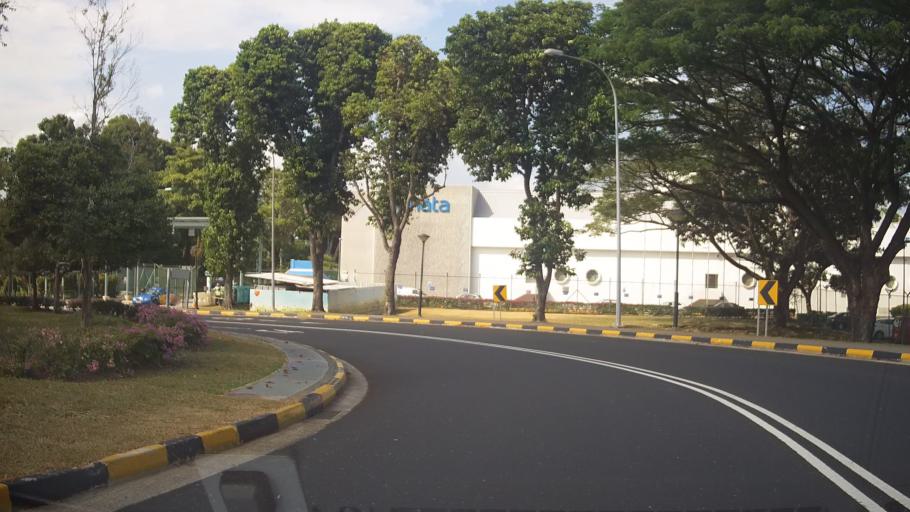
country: SG
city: Singapore
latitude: 1.3473
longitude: 103.9854
